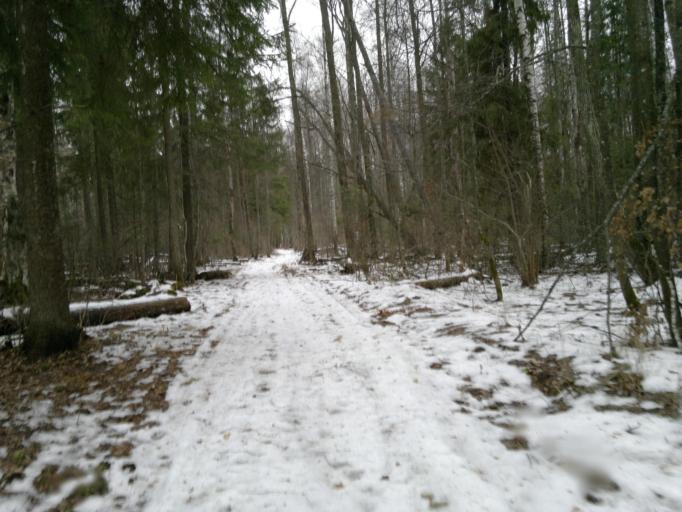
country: RU
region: Mariy-El
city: Yoshkar-Ola
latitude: 56.6095
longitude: 47.9558
